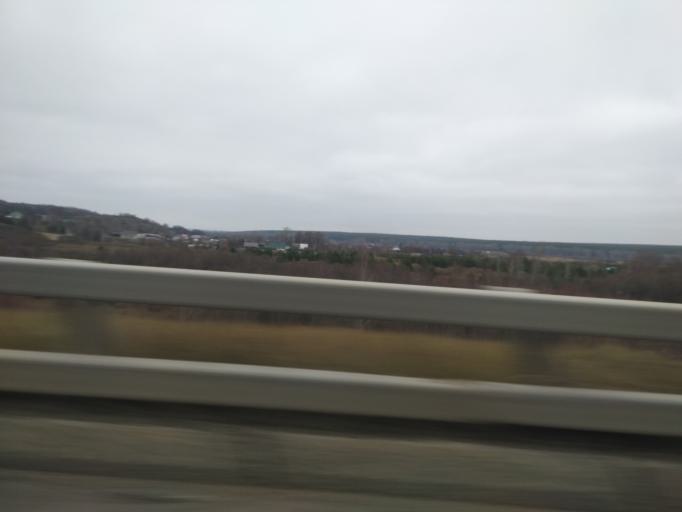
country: RU
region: Kirov
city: Sosnovka
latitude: 56.2342
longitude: 51.2218
